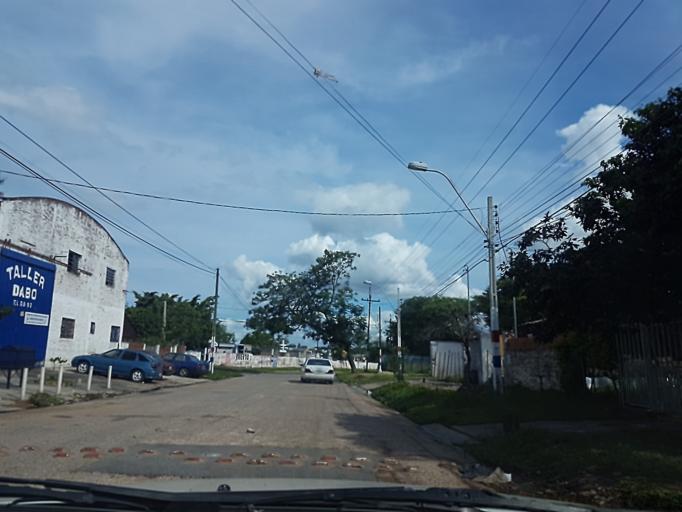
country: PY
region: Central
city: Colonia Mariano Roque Alonso
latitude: -25.2003
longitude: -57.5335
